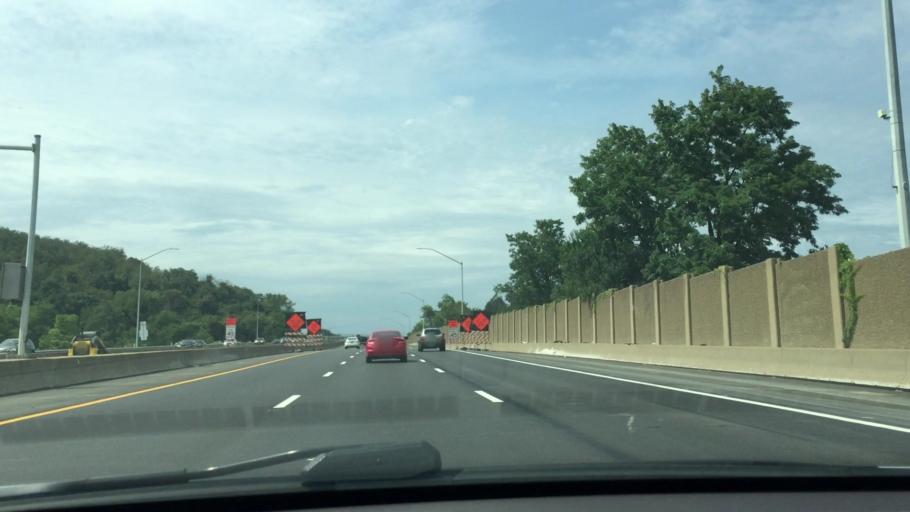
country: US
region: Pennsylvania
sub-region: Allegheny County
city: West View
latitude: 40.4936
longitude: -80.0137
